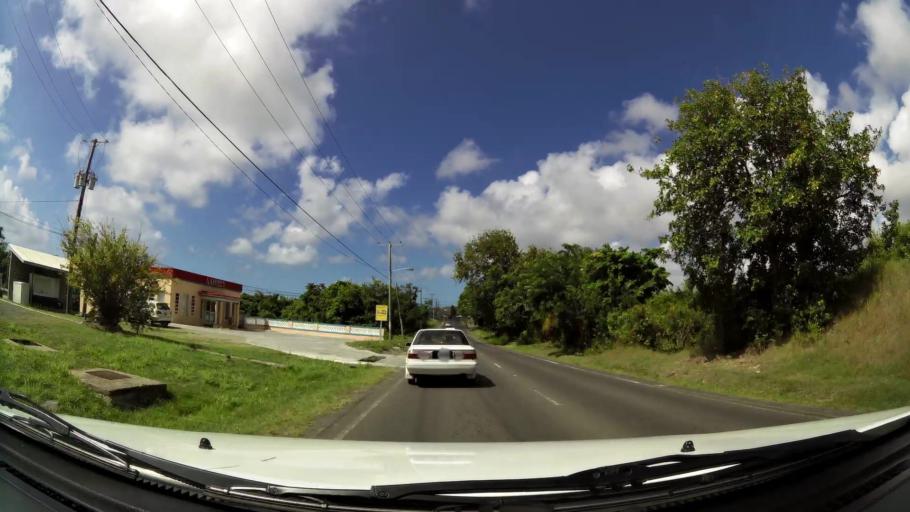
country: LC
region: Laborie Quarter
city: Laborie
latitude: 13.7370
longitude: -60.9705
